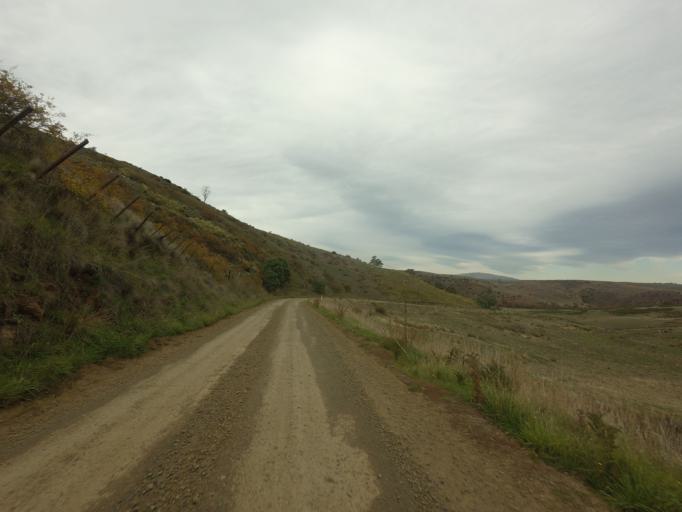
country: AU
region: Tasmania
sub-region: Derwent Valley
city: New Norfolk
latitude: -42.4018
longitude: 146.9483
